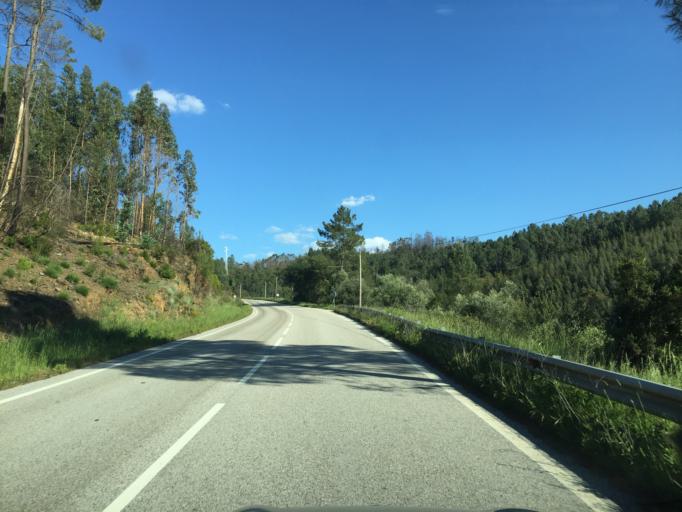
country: PT
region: Leiria
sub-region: Pedrogao Grande
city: Pedrogao Grande
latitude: 39.9865
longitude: -8.0783
